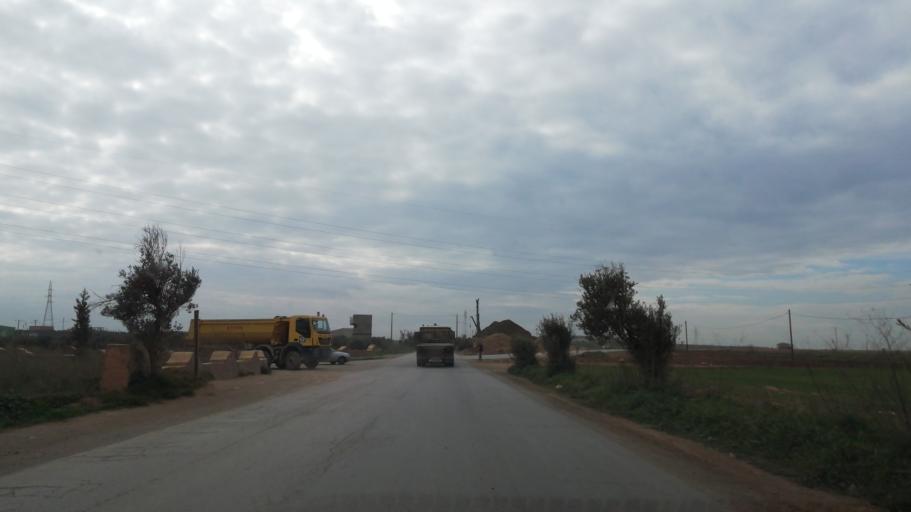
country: DZ
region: Oran
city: Ain el Bya
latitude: 35.7918
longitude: -0.3418
